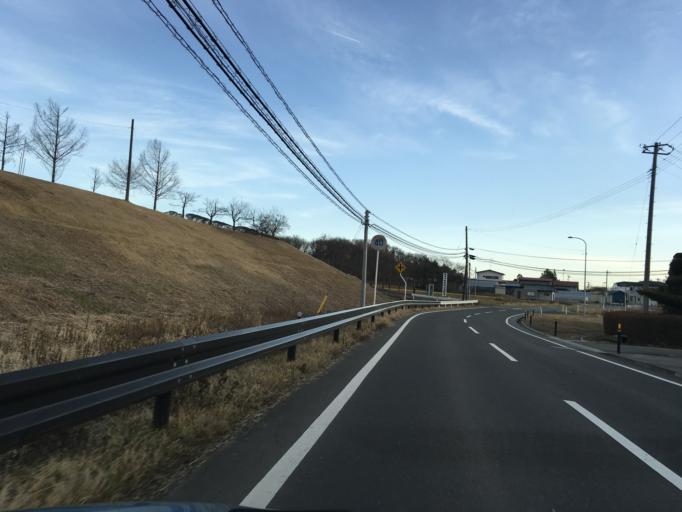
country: JP
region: Miyagi
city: Kogota
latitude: 38.6848
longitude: 141.0956
